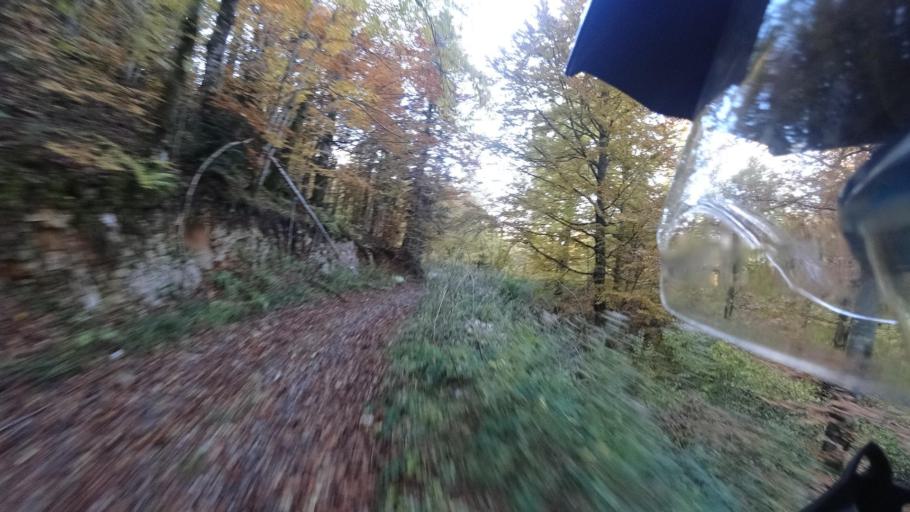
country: HR
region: Karlovacka
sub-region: Grad Ogulin
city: Ogulin
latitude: 45.1737
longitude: 15.1459
